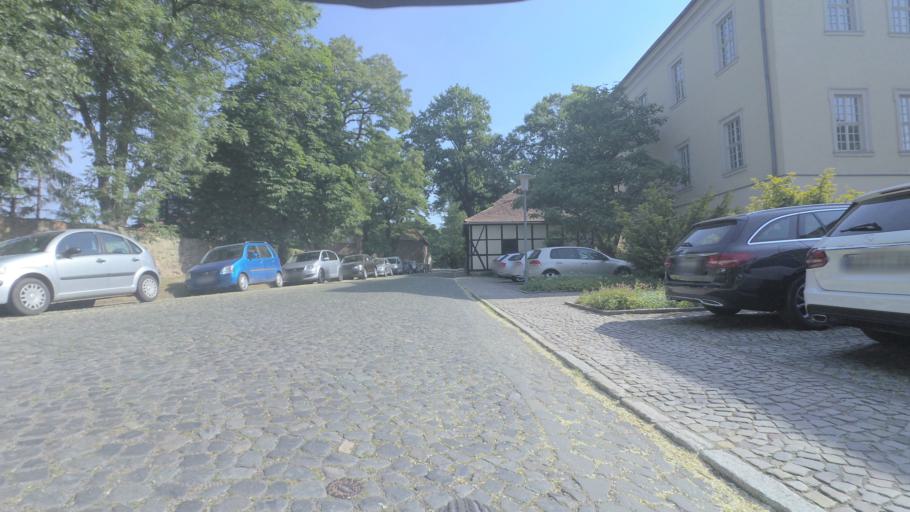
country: DE
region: Saxony-Anhalt
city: Hoym
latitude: 51.7850
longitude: 11.3150
